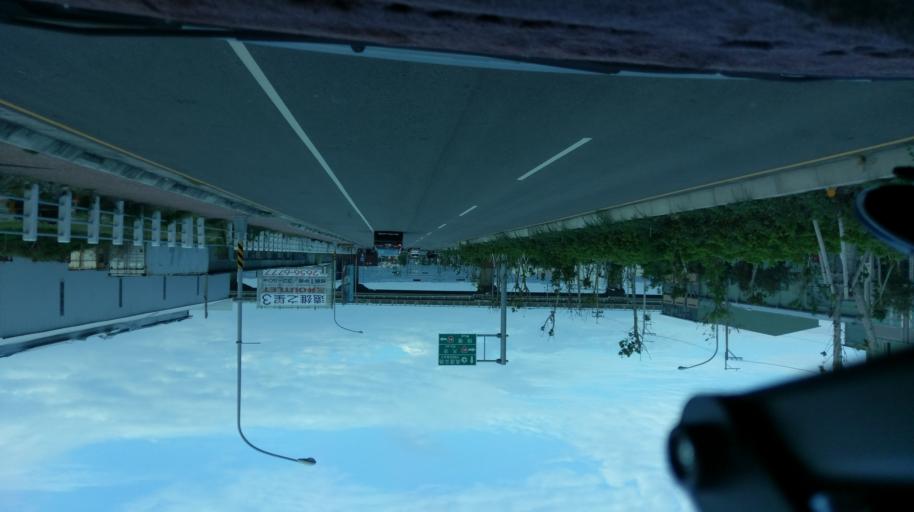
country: TW
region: Taiwan
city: Fengyuan
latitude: 24.2955
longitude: 120.5513
